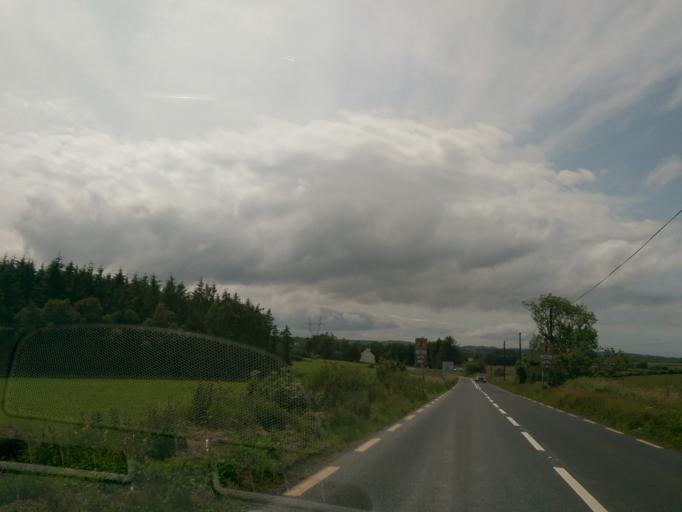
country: IE
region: Munster
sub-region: An Clar
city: Kilrush
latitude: 52.6976
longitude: -9.3361
